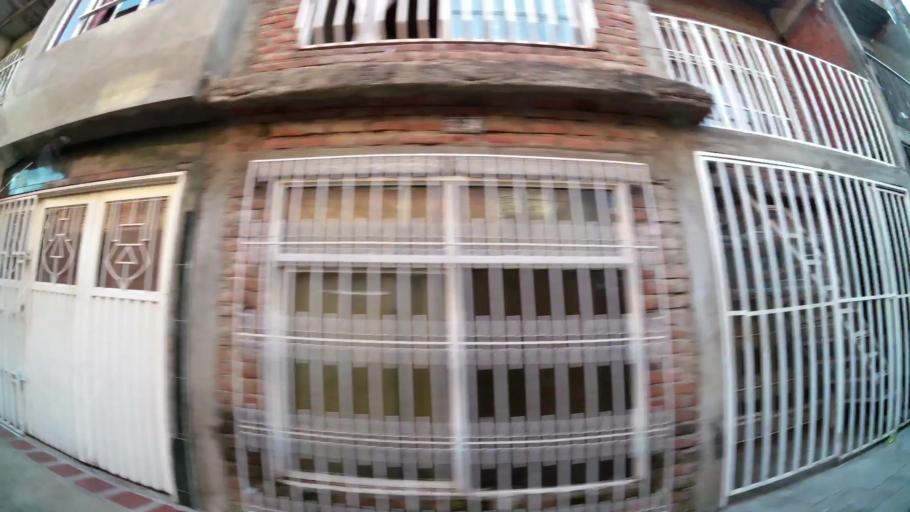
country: CO
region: Valle del Cauca
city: Cali
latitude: 3.4079
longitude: -76.5003
